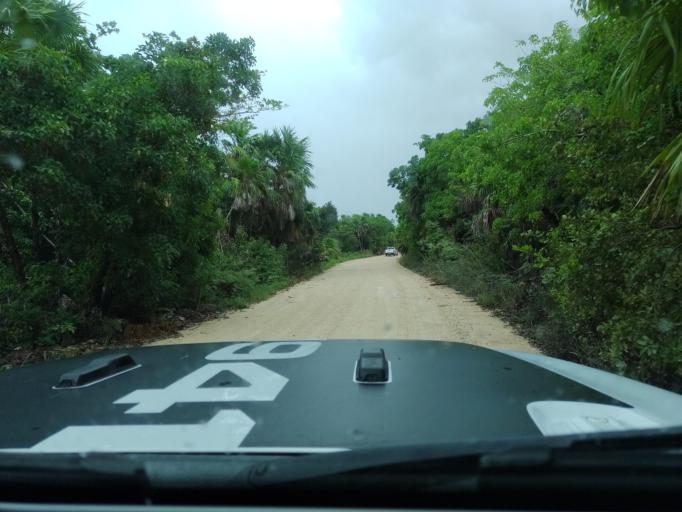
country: MX
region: Quintana Roo
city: Tulum
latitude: 20.0566
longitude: -87.4810
